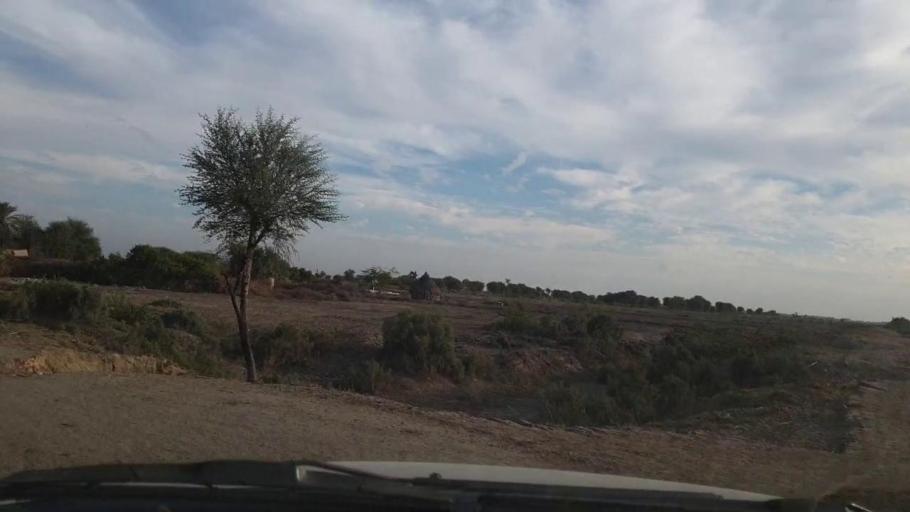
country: PK
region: Sindh
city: Pithoro
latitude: 25.6439
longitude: 69.2757
